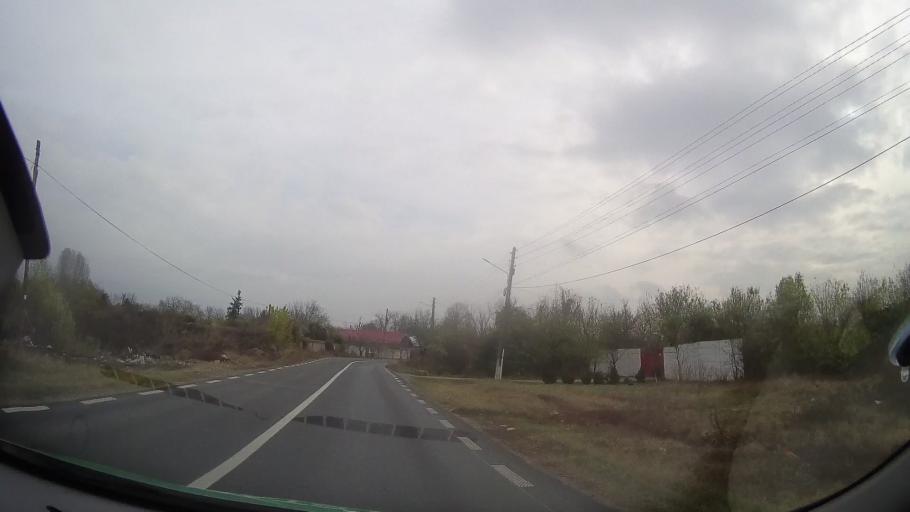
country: RO
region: Ilfov
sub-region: Comuna Gruiu
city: Lipia
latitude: 44.7175
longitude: 26.2730
